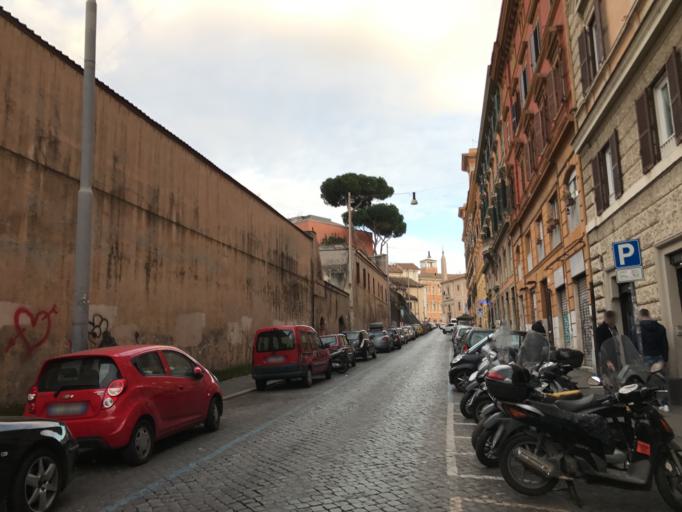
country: IT
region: Latium
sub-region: Citta metropolitana di Roma Capitale
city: Rome
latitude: 41.8879
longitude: 12.5013
